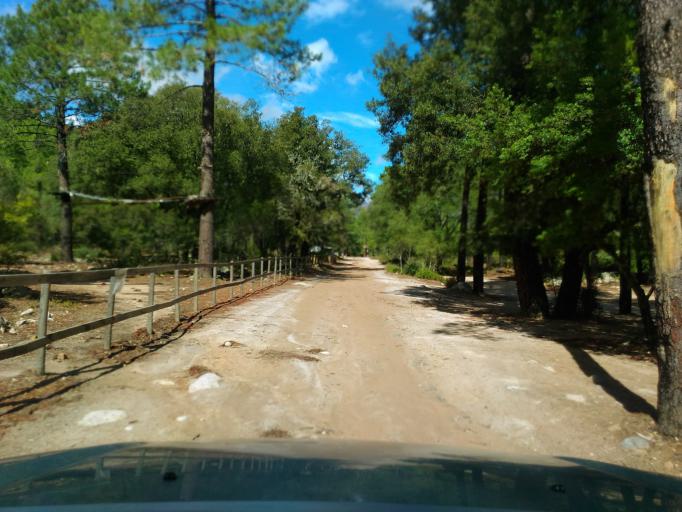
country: FR
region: Corsica
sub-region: Departement de la Corse-du-Sud
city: Porto-Vecchio
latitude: 41.7202
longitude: 9.3010
